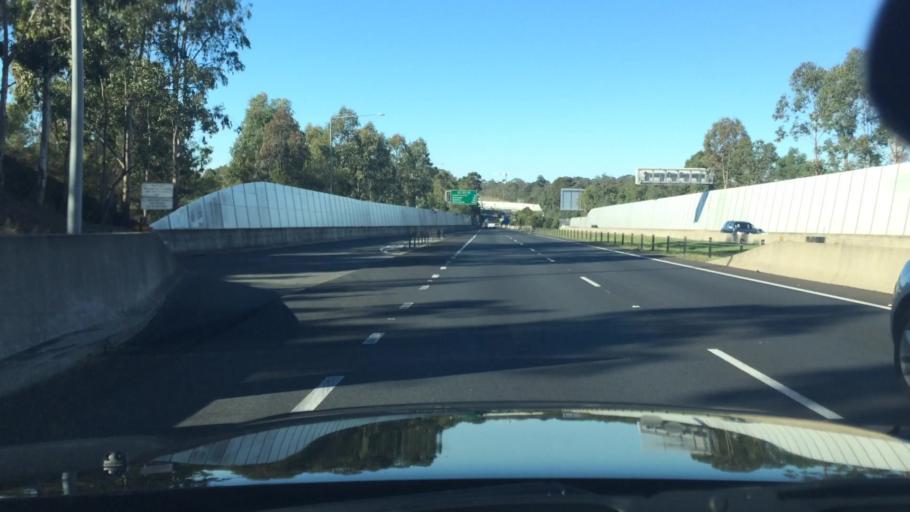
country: AU
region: New South Wales
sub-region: Parramatta
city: Northmead
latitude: -33.7608
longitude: 150.9603
